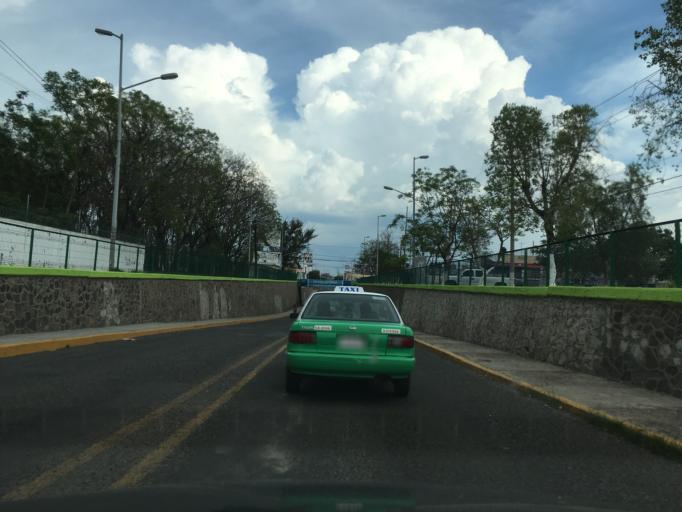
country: MX
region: Guanajuato
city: Celaya
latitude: 20.5333
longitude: -100.8191
